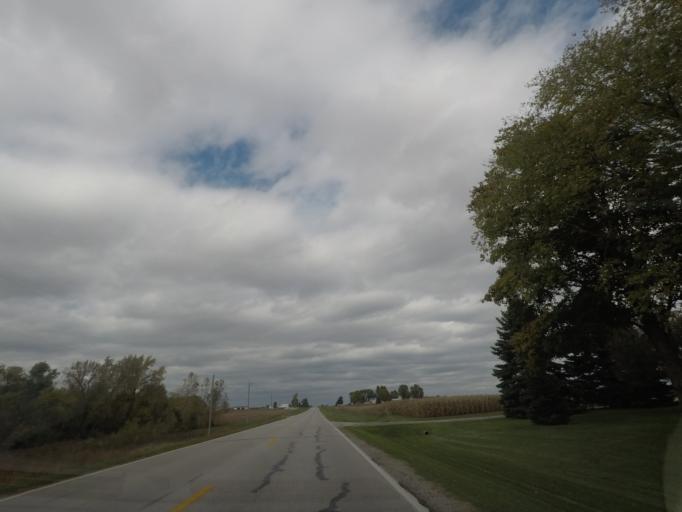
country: US
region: Iowa
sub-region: Story County
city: Huxley
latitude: 41.8429
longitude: -93.5315
